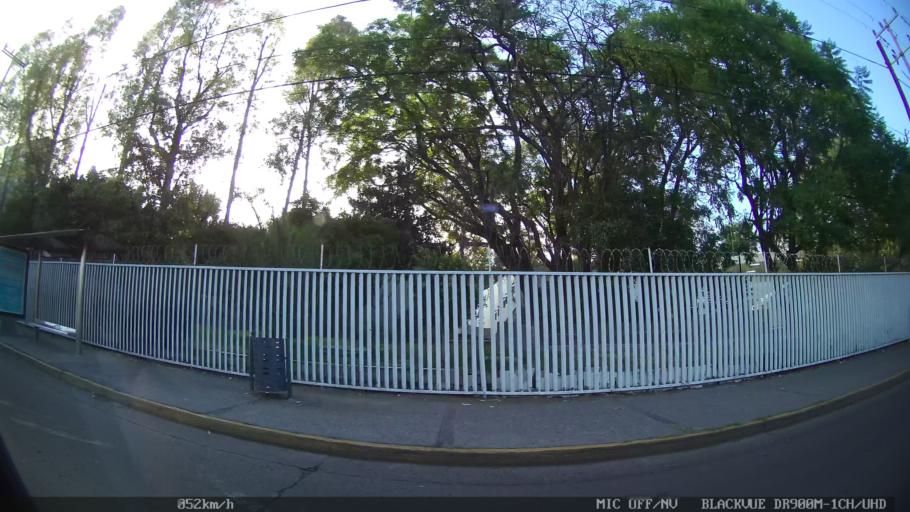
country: MX
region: Jalisco
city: Tlaquepaque
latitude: 20.6542
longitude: -103.3238
